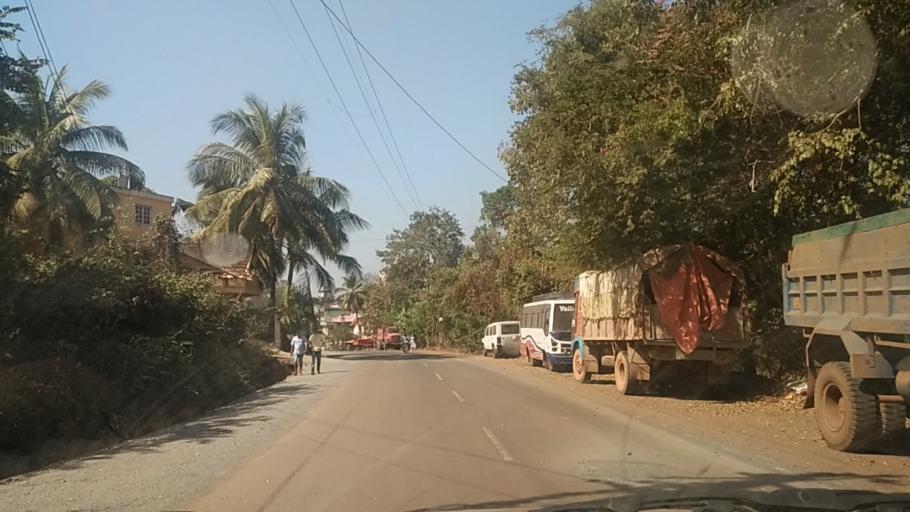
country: IN
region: Goa
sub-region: South Goa
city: Raia
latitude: 15.2995
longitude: 73.9666
